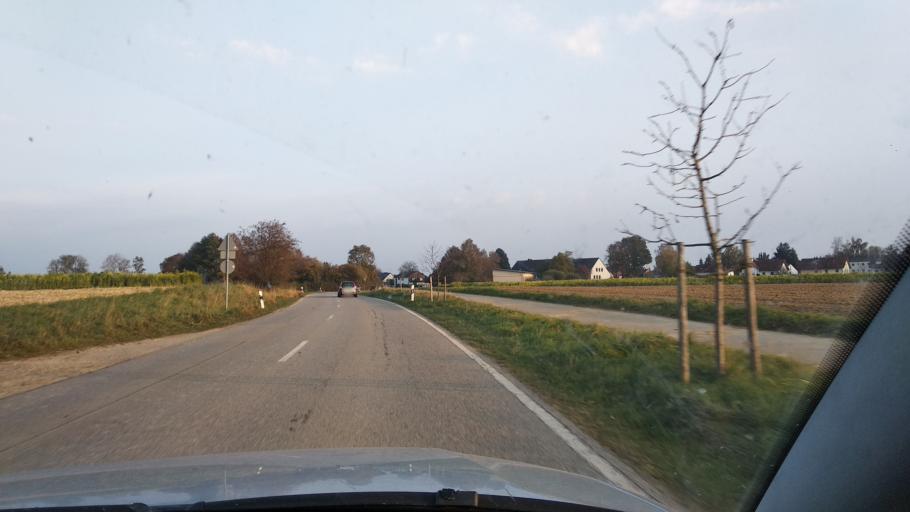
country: DE
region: Bavaria
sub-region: Upper Bavaria
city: Anzing
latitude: 48.1570
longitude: 11.8458
